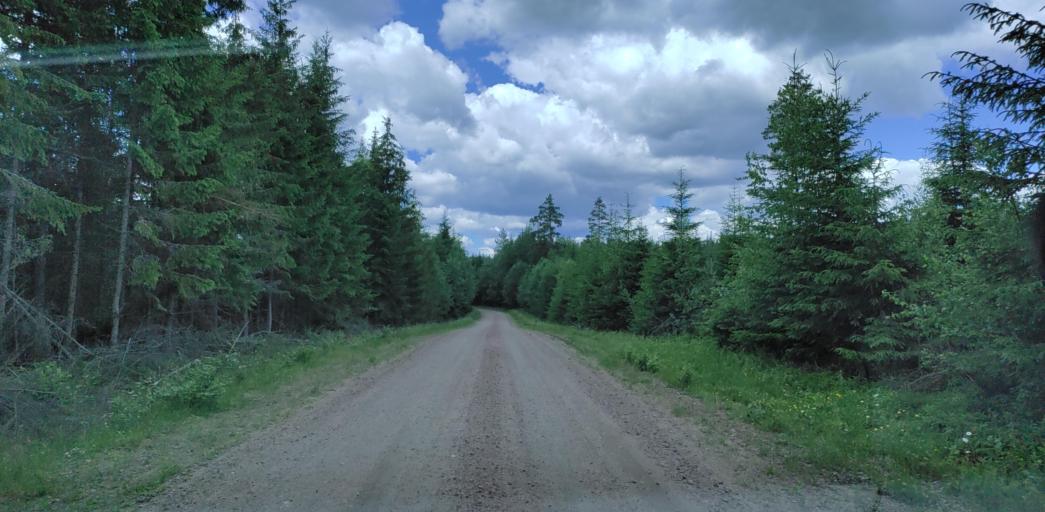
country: SE
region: Vaermland
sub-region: Hagfors Kommun
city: Ekshaerad
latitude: 60.0862
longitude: 13.4382
